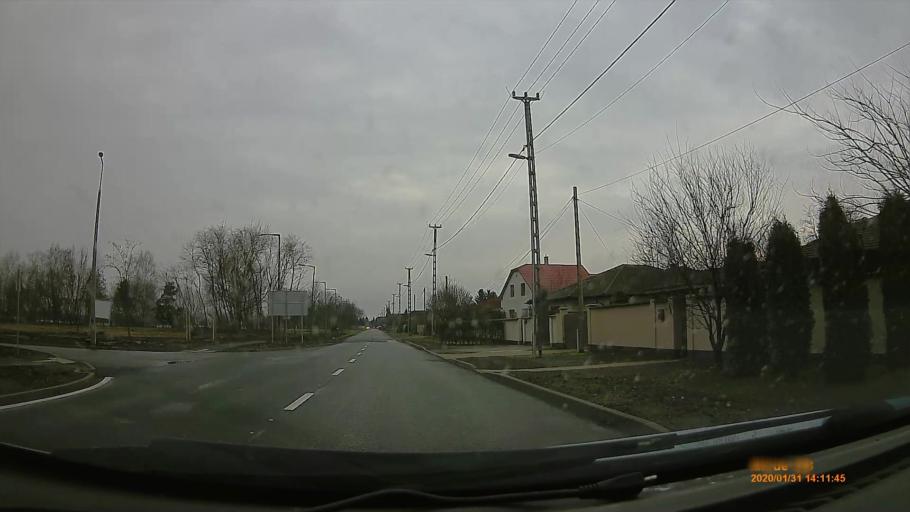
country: HU
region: Szabolcs-Szatmar-Bereg
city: Nyiregyhaza
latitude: 47.9562
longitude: 21.6770
